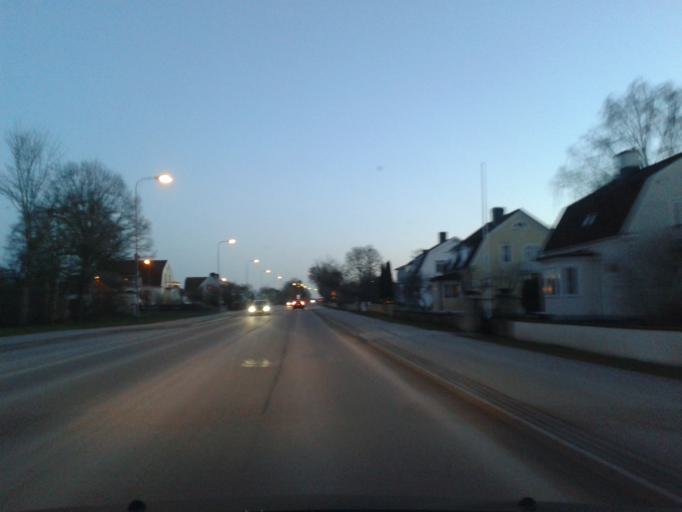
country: SE
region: Gotland
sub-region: Gotland
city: Visby
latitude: 57.6317
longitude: 18.3124
